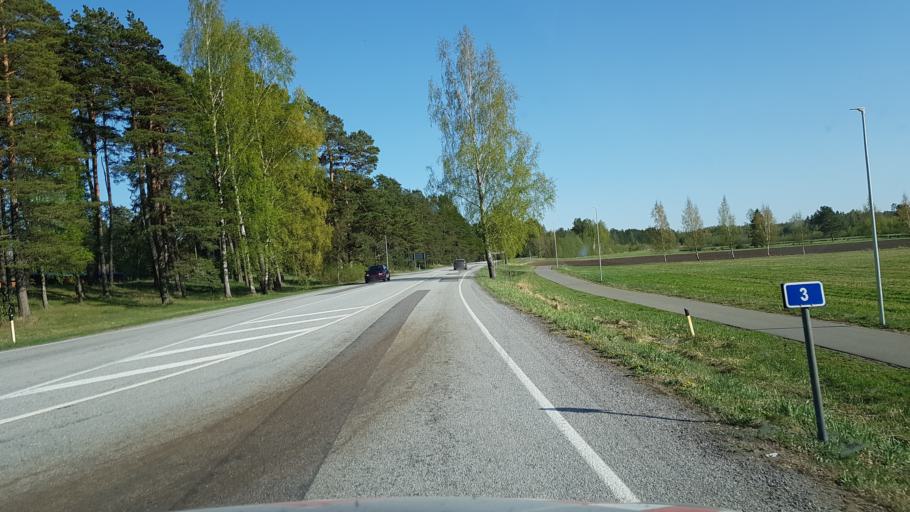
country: EE
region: Paernumaa
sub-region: Paikuse vald
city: Paikuse
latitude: 58.3576
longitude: 24.6601
